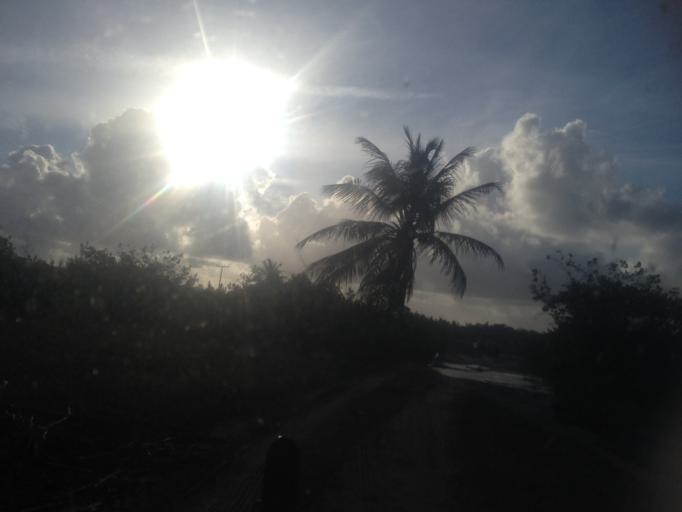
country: BR
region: Sergipe
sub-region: Indiaroba
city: Indiaroba
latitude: -11.4664
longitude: -37.3567
